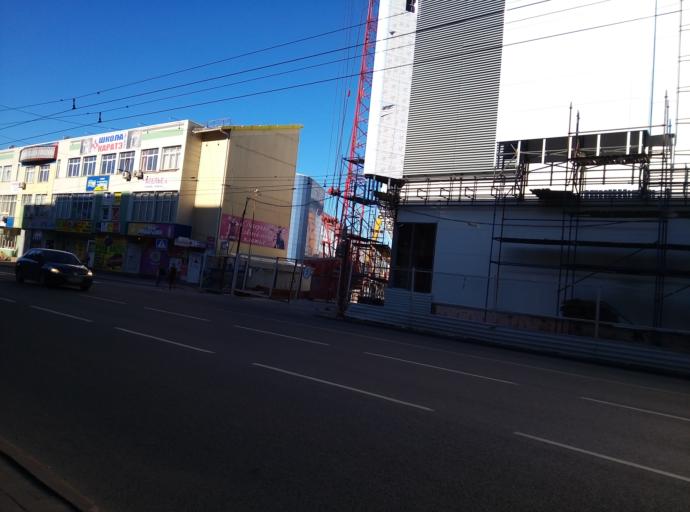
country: RU
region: Kursk
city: Kursk
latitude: 51.7488
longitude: 36.1902
